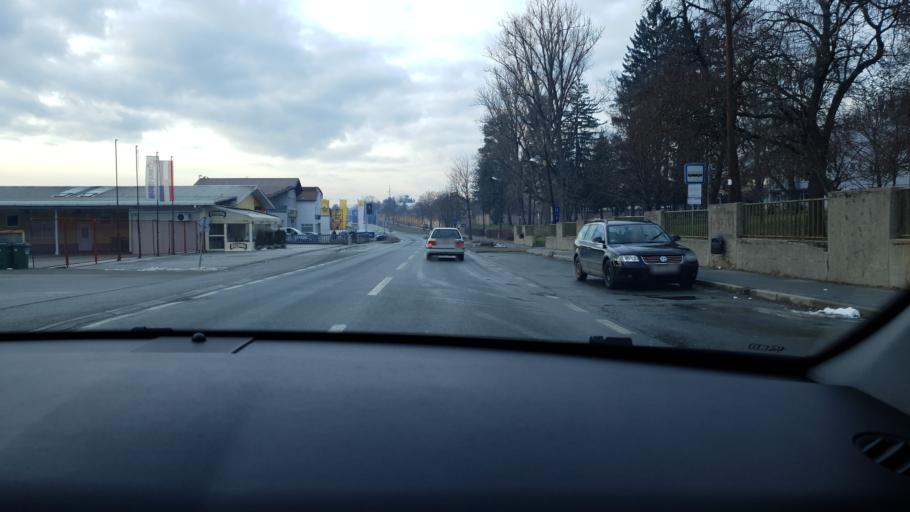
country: HR
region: Pozesko-Slavonska
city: Pozega
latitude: 45.3428
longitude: 17.6981
